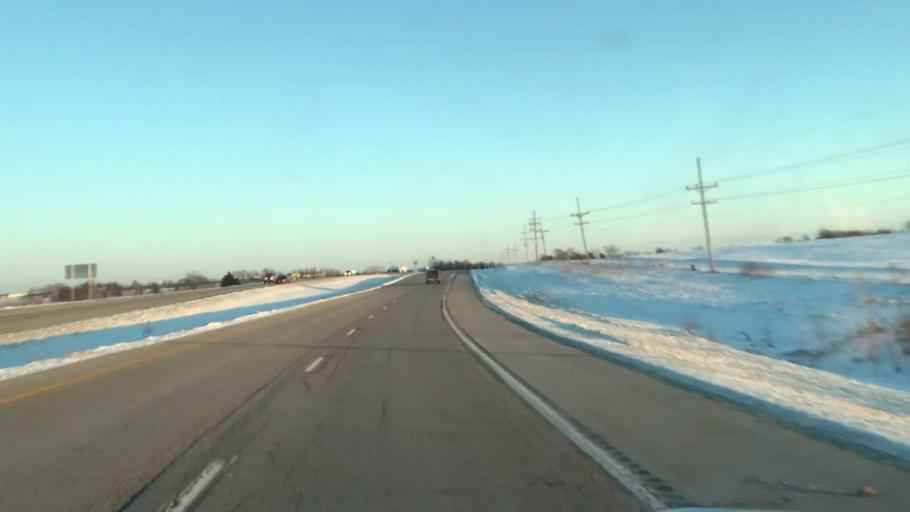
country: US
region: Missouri
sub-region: Clinton County
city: Cameron
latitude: 39.7602
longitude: -94.3491
